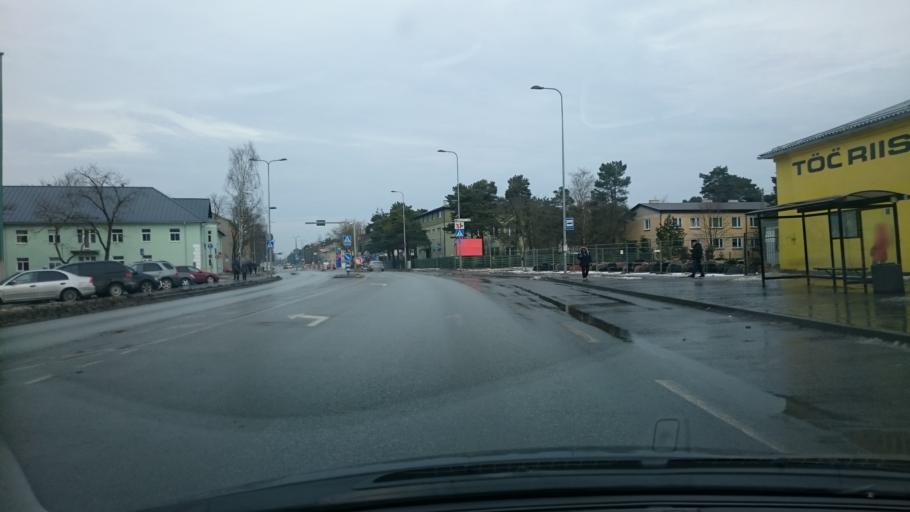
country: EE
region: Harju
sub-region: Tallinna linn
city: Tallinn
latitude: 59.3731
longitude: 24.7179
